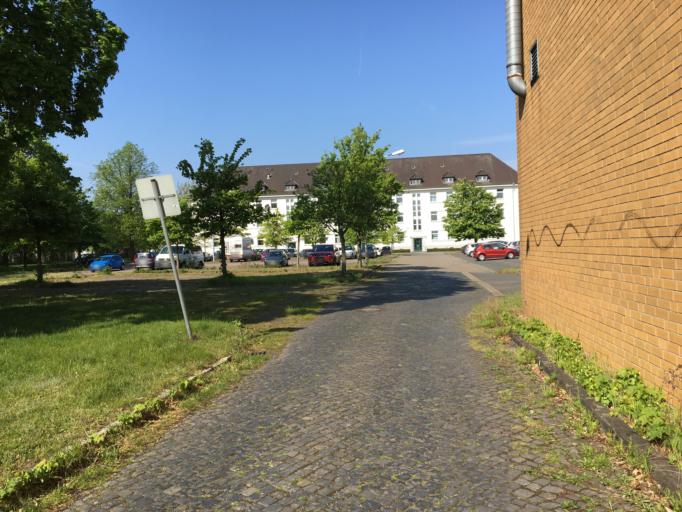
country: DE
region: Lower Saxony
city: Braunschweig
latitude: 52.2840
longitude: 10.5401
